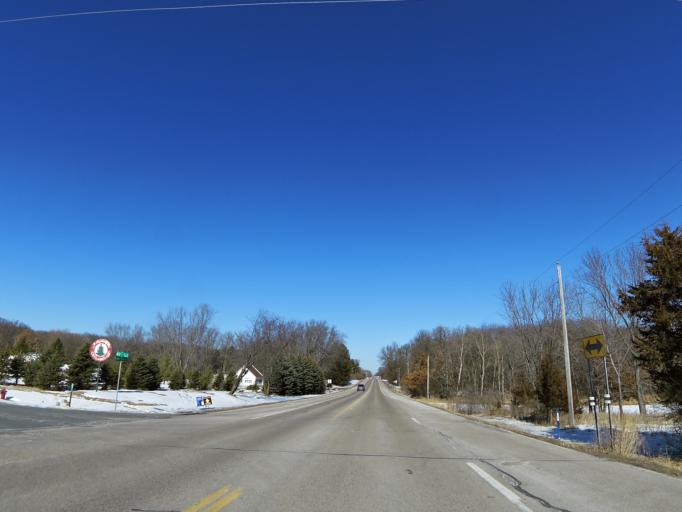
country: US
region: Minnesota
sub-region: Washington County
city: Lake Elmo
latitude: 45.0116
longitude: -92.8832
